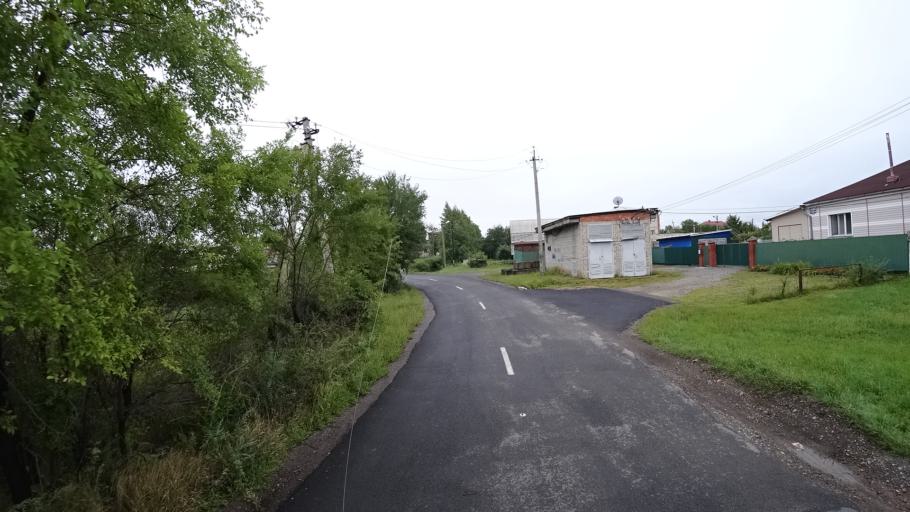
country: RU
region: Primorskiy
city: Monastyrishche
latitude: 44.2006
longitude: 132.4460
